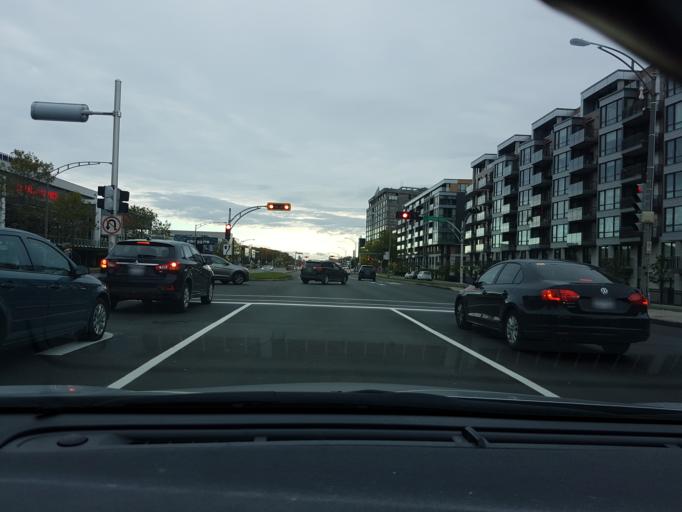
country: CA
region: Quebec
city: L'Ancienne-Lorette
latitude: 46.7712
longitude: -71.2806
